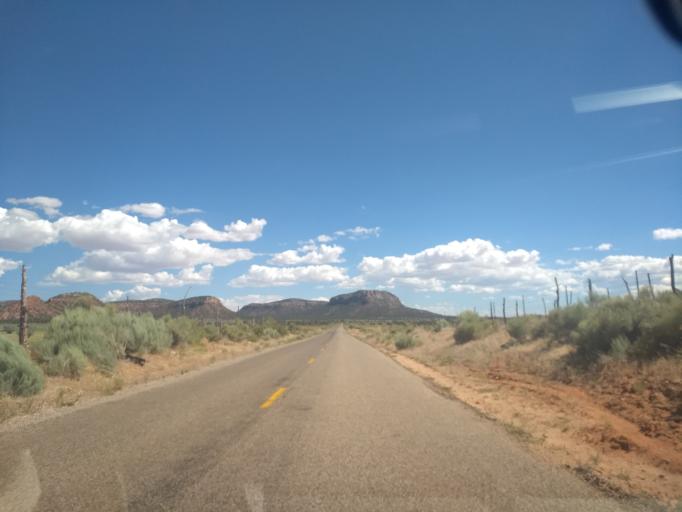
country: US
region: Utah
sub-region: Washington County
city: Hildale
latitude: 36.9592
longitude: -112.8746
